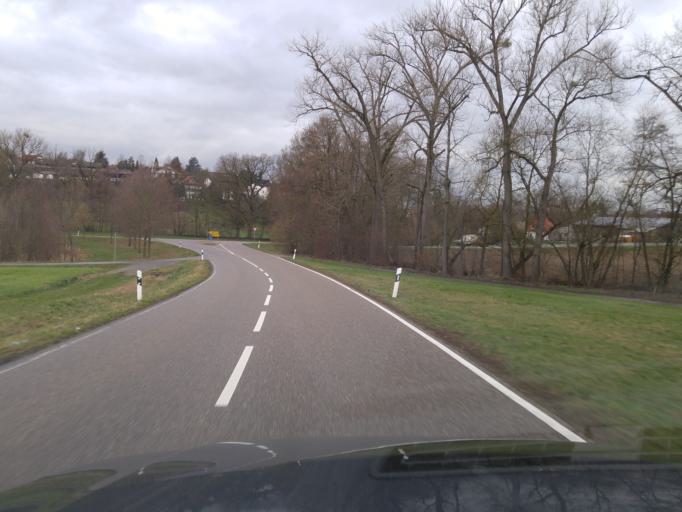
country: DE
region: Baden-Wuerttemberg
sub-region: Regierungsbezirk Stuttgart
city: Ohringen
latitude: 49.1950
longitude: 9.5322
